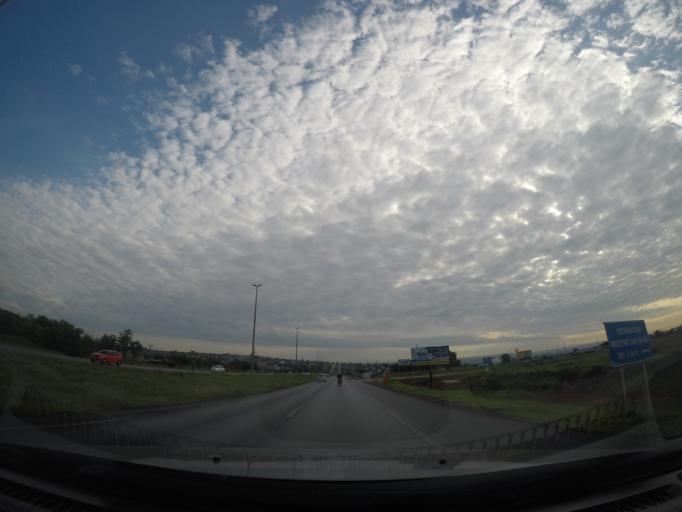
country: BR
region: Goias
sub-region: Planaltina
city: Planaltina
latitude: -15.6112
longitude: -47.6987
